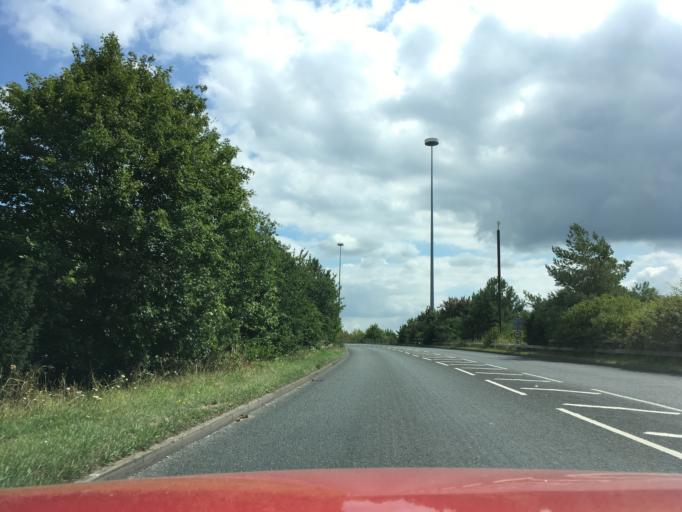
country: GB
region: England
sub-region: Gloucestershire
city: Gloucester
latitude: 51.8625
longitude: -2.2320
